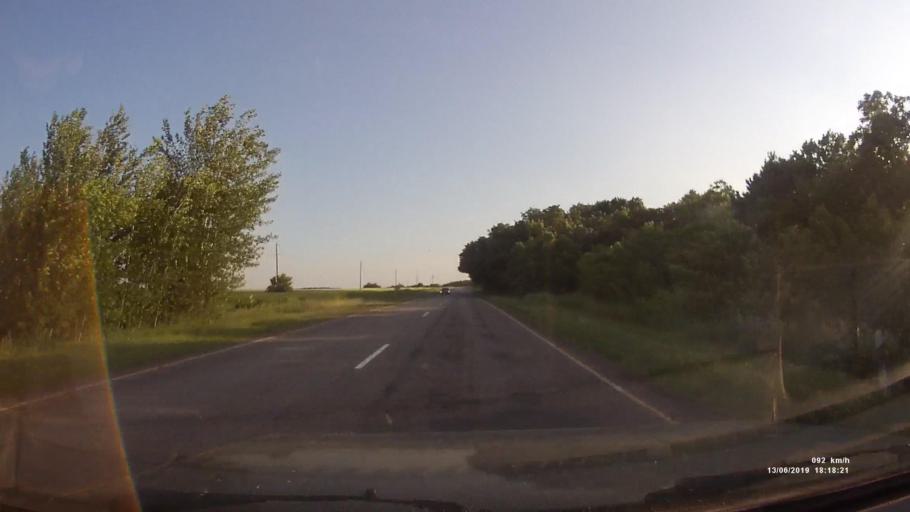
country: RU
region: Rostov
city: Kazanskaya
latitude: 49.9090
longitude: 41.3149
